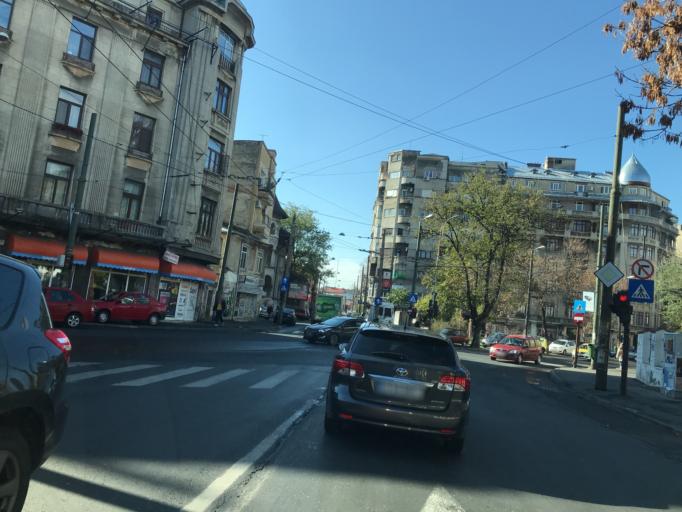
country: RO
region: Bucuresti
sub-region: Municipiul Bucuresti
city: Bucuresti
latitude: 44.4446
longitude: 26.0884
